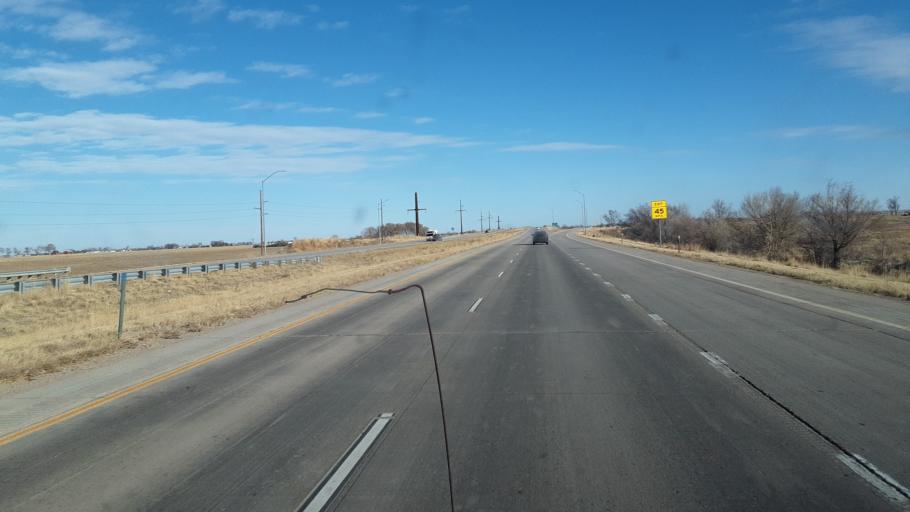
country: US
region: Colorado
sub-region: Morgan County
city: Brush
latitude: 40.2678
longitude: -103.7058
